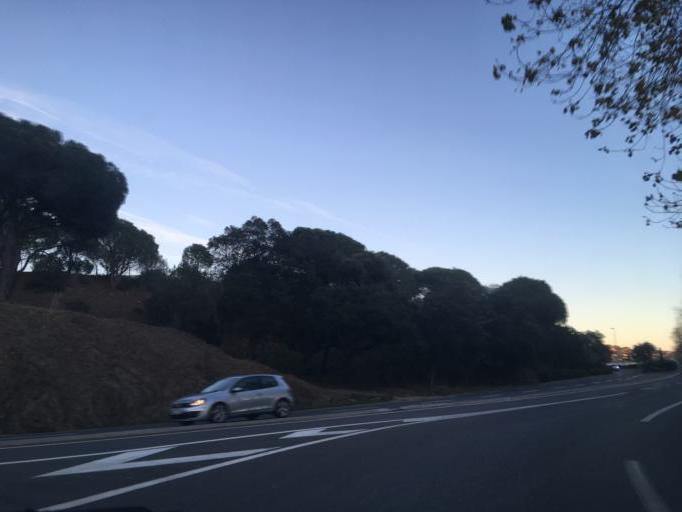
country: FR
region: Provence-Alpes-Cote d'Azur
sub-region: Departement du Var
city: Sainte-Maxime
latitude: 43.3277
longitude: 6.6143
